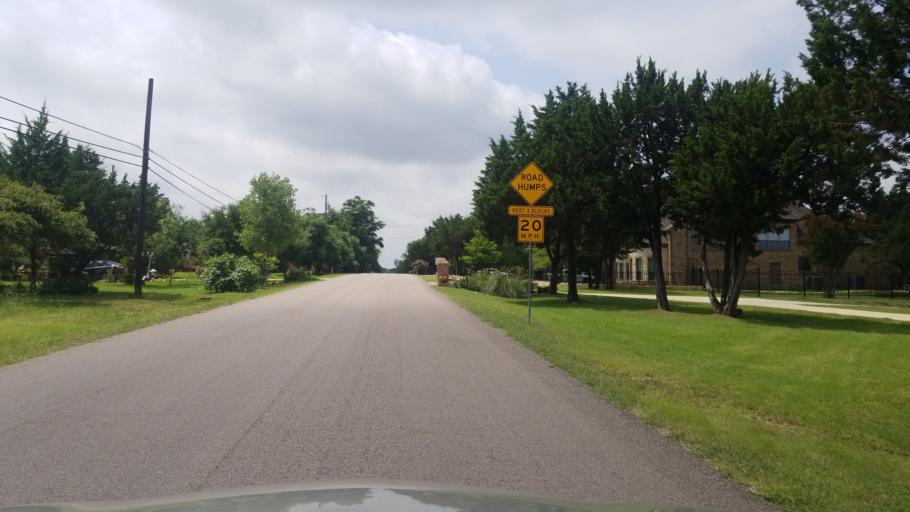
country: US
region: Texas
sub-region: Dallas County
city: Duncanville
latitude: 32.6842
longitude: -96.9341
